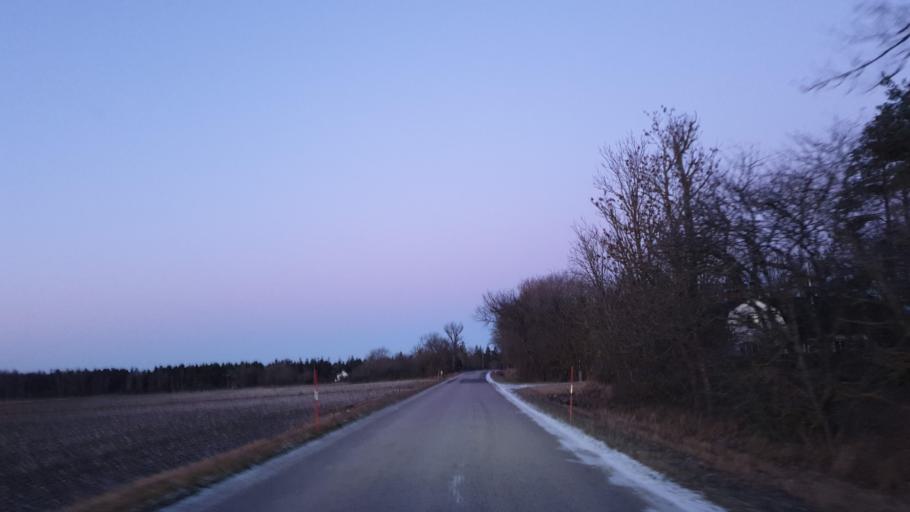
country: SE
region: Gotland
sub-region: Gotland
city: Slite
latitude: 57.4072
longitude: 18.8054
